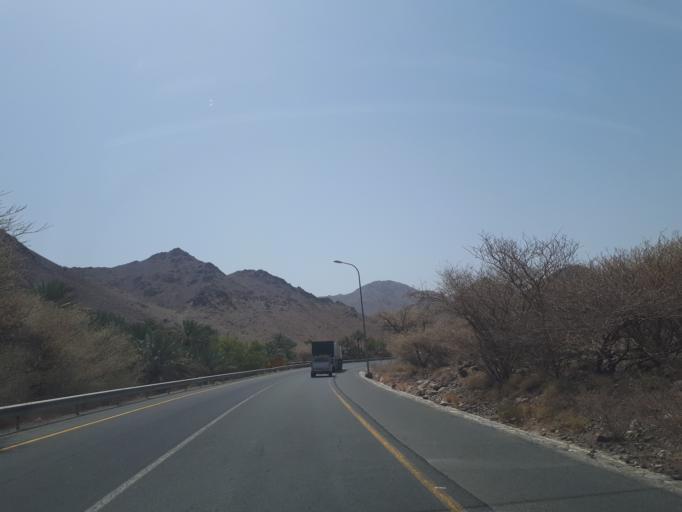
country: OM
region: Muhafazat ad Dakhiliyah
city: Sufalat Sama'il
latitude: 23.2281
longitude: 58.0790
